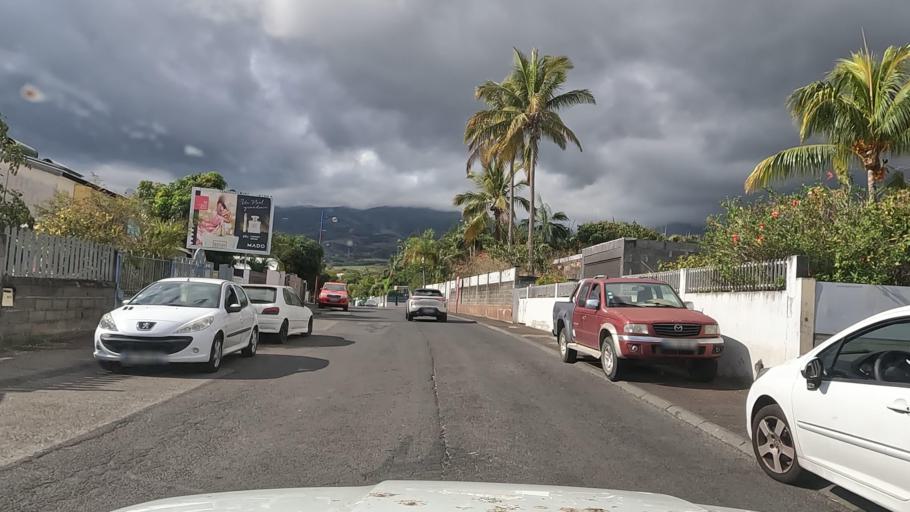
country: RE
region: Reunion
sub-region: Reunion
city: Saint-Louis
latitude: -21.2770
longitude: 55.4049
